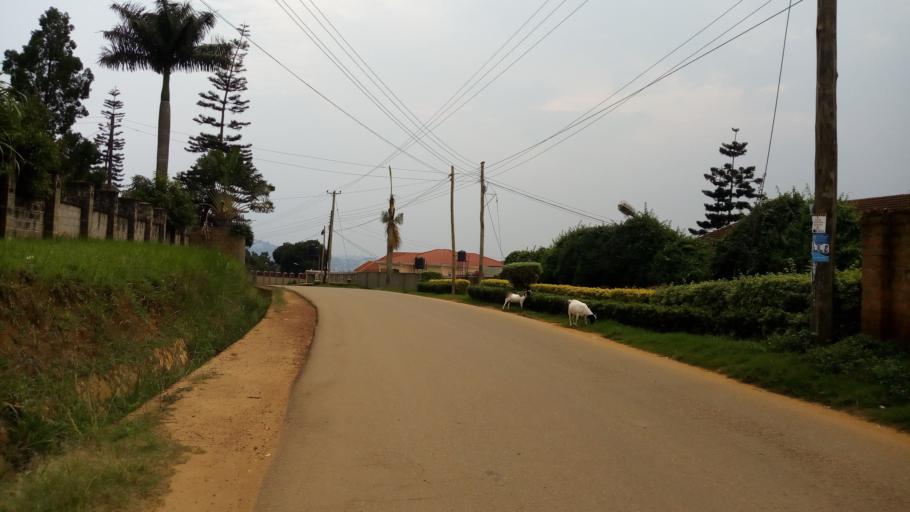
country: UG
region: Central Region
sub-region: Wakiso District
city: Kireka
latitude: 0.3183
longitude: 32.6411
